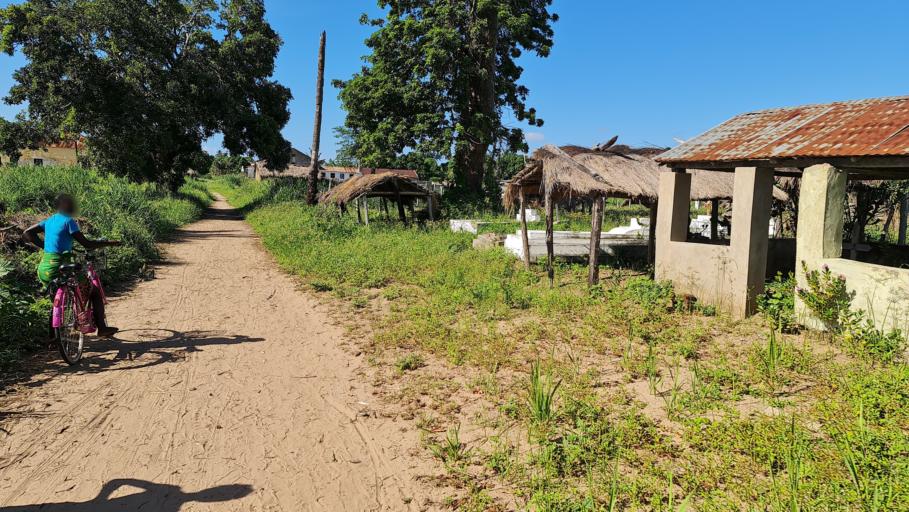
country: MZ
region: Zambezia
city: Quelimane
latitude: -17.4429
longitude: 37.6988
